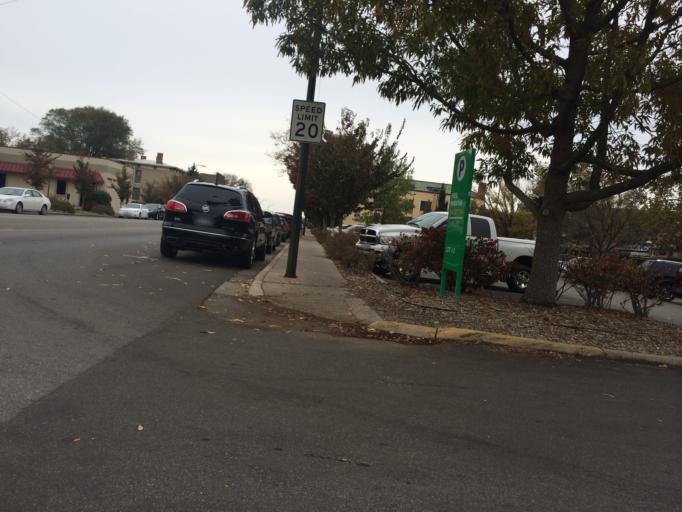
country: US
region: Kansas
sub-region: Douglas County
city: Lawrence
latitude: 38.9679
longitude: -95.2370
